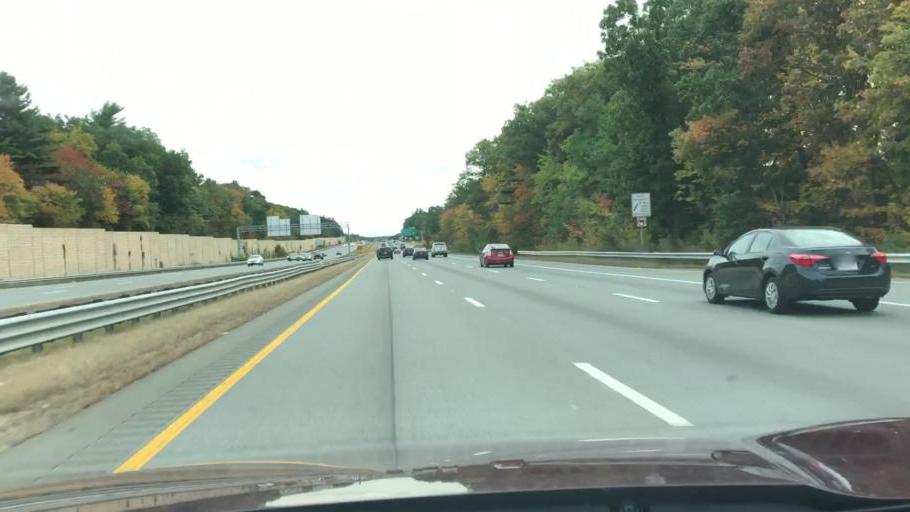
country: US
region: Massachusetts
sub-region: Essex County
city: Andover
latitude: 42.6311
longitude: -71.1799
